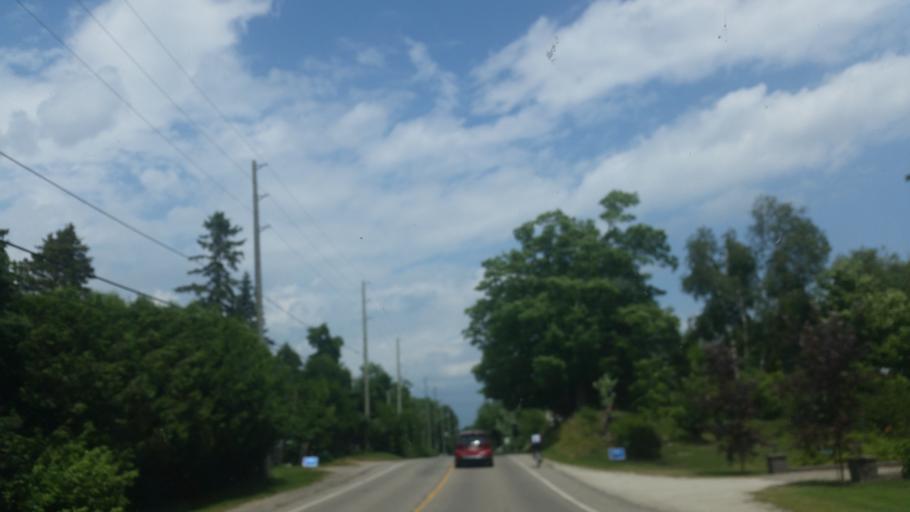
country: CA
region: Ontario
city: Orangeville
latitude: 43.7915
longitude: -80.0174
